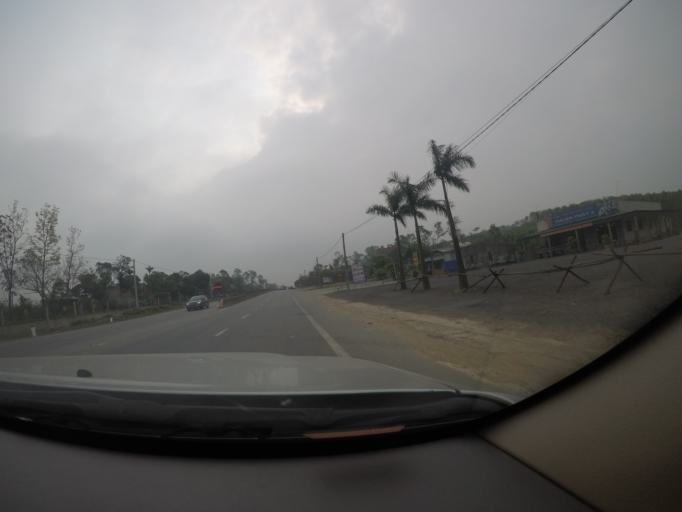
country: VN
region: Ha Tinh
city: Cam Xuyen
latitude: 18.2040
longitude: 106.1422
